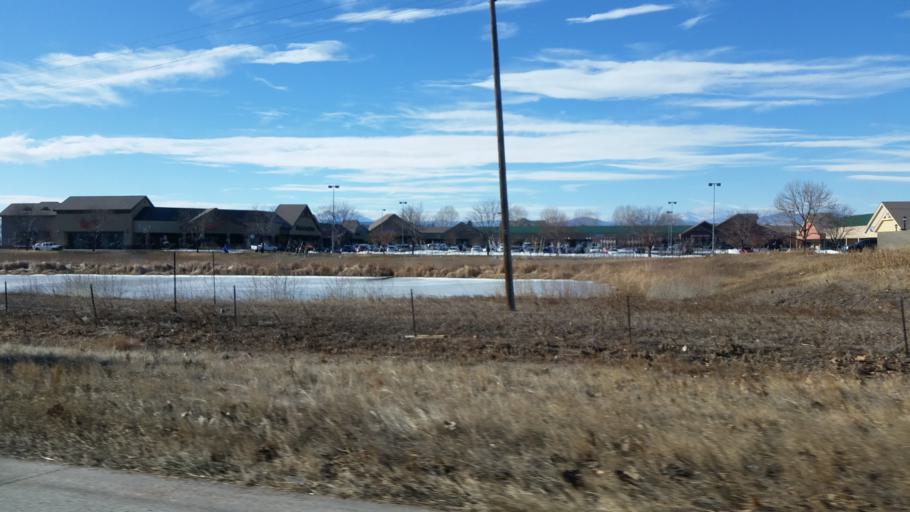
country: US
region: Colorado
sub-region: Larimer County
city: Loveland
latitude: 40.4098
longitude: -104.9934
